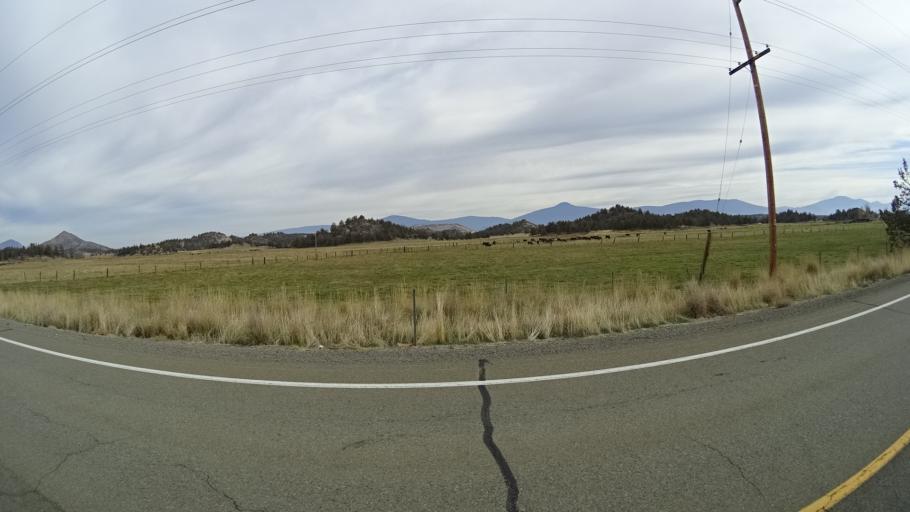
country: US
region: California
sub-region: Siskiyou County
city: Montague
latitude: 41.6756
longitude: -122.5262
